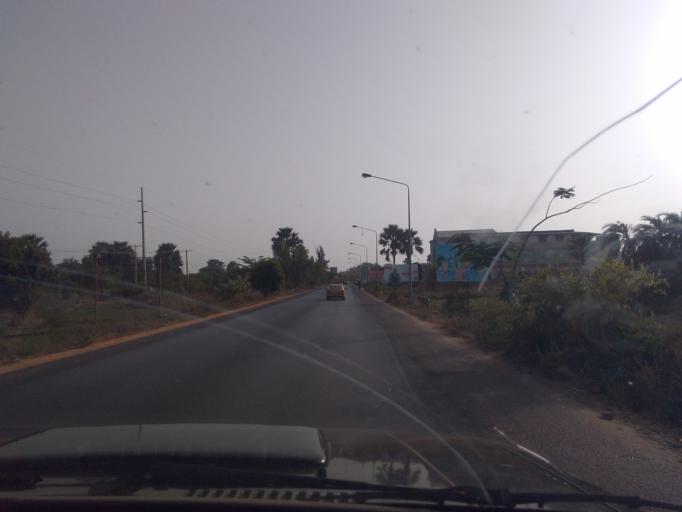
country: GM
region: Banjul
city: Bakau
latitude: 13.4593
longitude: -16.6963
